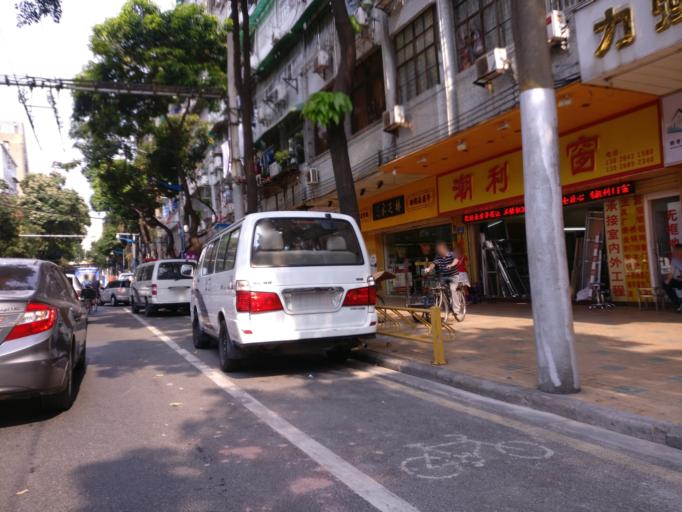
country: CN
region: Guangdong
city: Guangzhou
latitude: 23.1244
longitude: 113.2822
